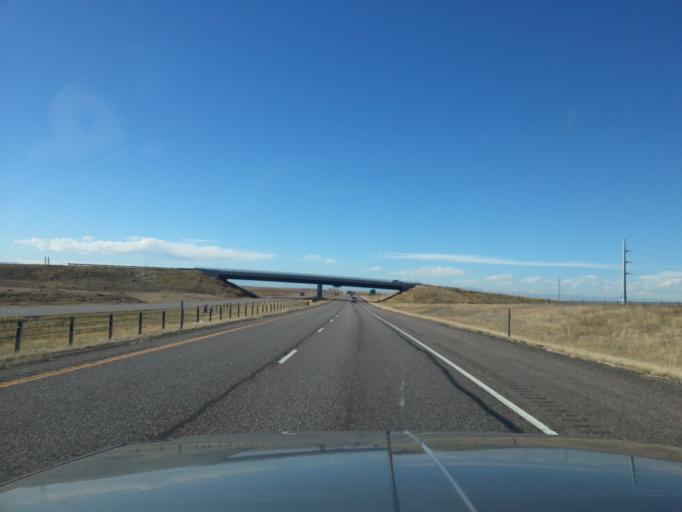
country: US
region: Colorado
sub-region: Adams County
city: Brighton
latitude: 39.9053
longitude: -104.7687
